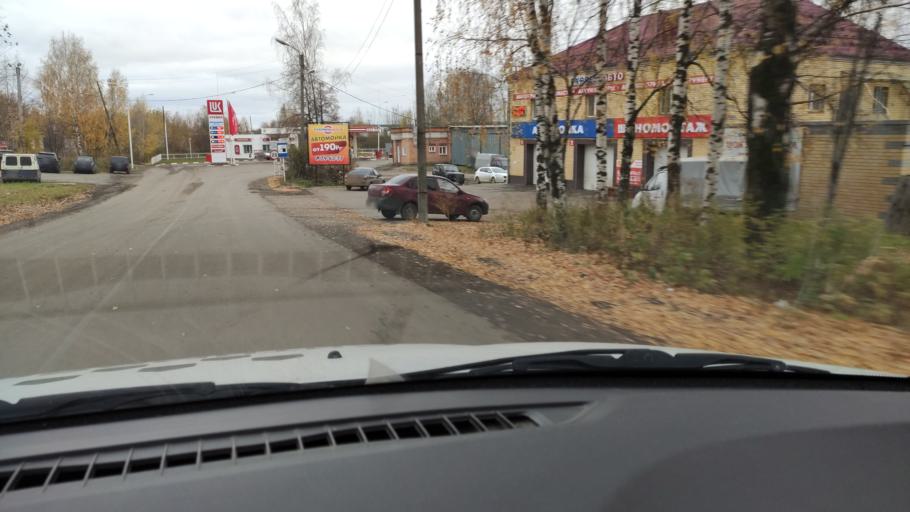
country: RU
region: Kirov
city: Slobodskoy
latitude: 58.7199
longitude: 50.1750
